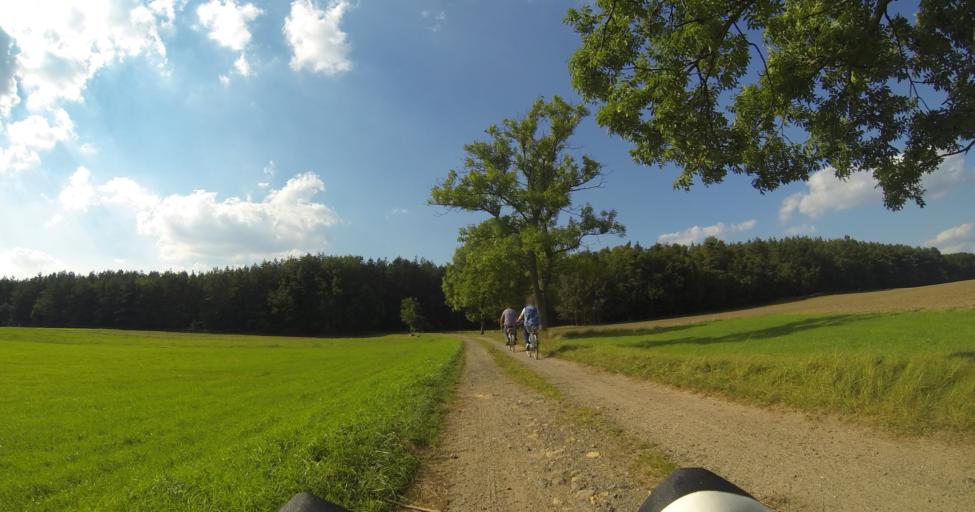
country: DE
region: Saxony
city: Ebersbach
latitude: 51.1971
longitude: 13.6630
